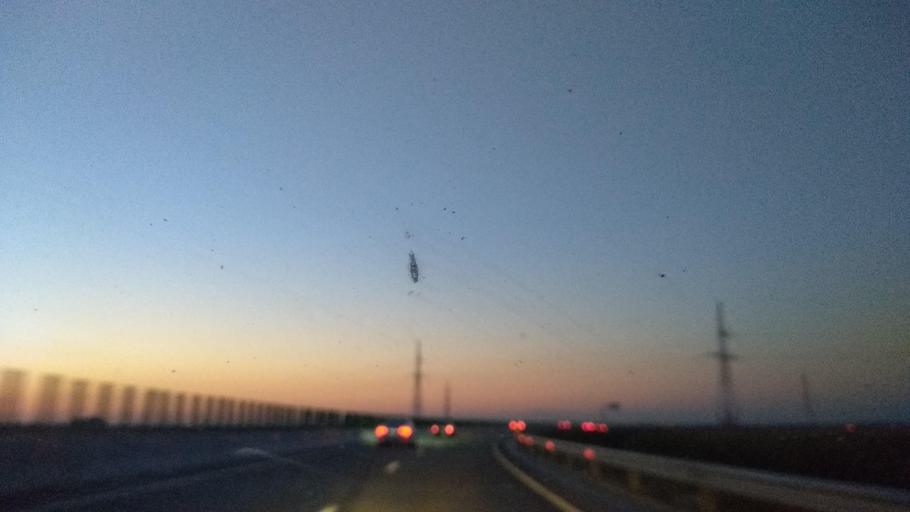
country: RO
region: Giurgiu
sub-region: Comuna Fratesti
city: Remus
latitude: 43.9553
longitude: 25.9852
